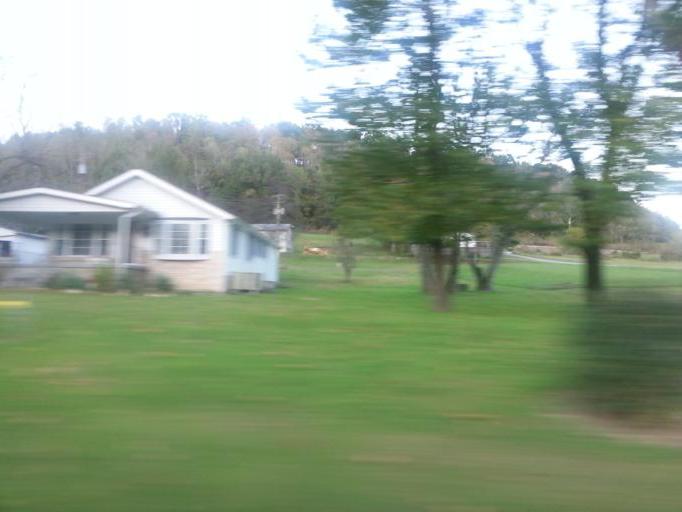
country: US
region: Tennessee
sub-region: Anderson County
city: Rocky Top
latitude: 36.2586
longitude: -84.1842
